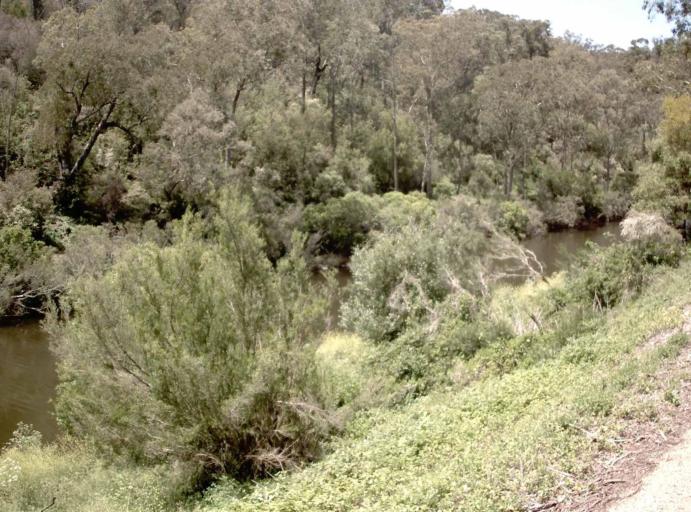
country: AU
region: Victoria
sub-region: East Gippsland
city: Lakes Entrance
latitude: -37.5444
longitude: 147.8659
